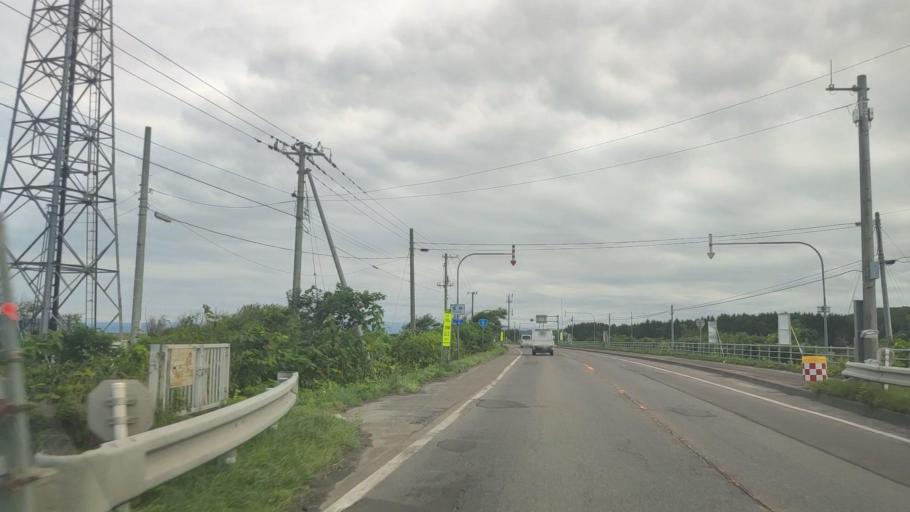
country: JP
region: Hokkaido
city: Niseko Town
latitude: 42.4341
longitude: 140.3201
